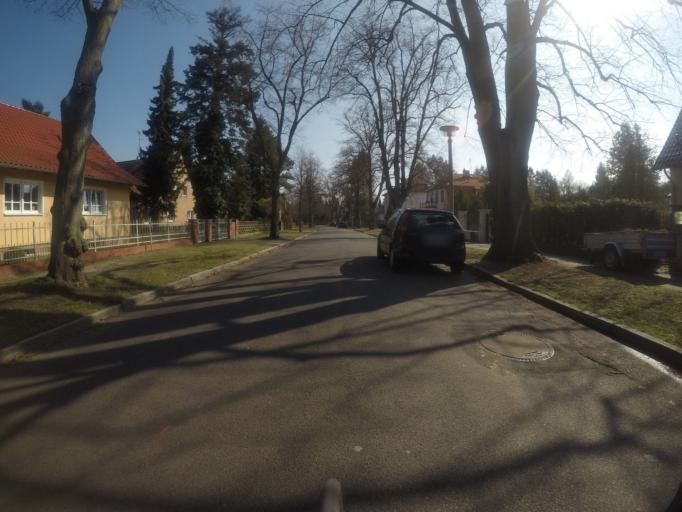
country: DE
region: Brandenburg
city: Konigs Wusterhausen
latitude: 52.2956
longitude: 13.6578
